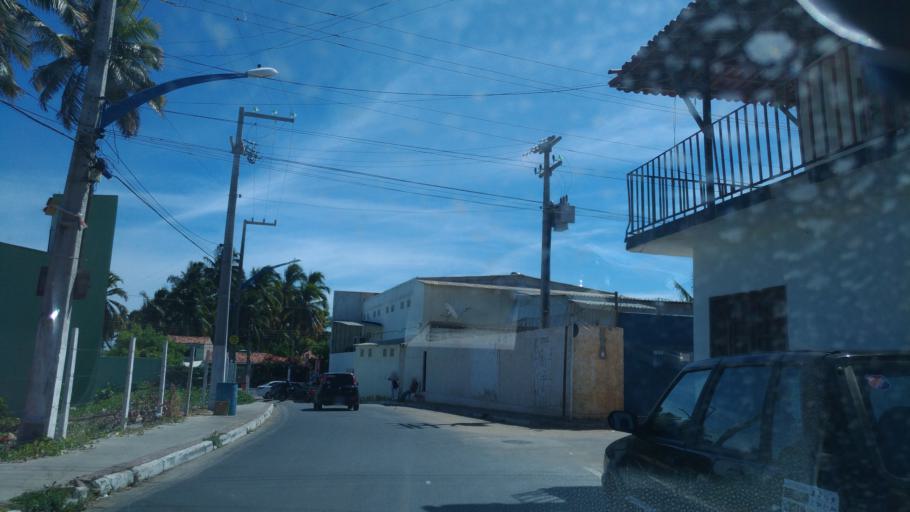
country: BR
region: Alagoas
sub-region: Marechal Deodoro
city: Marechal Deodoro
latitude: -9.7690
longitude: -35.8441
